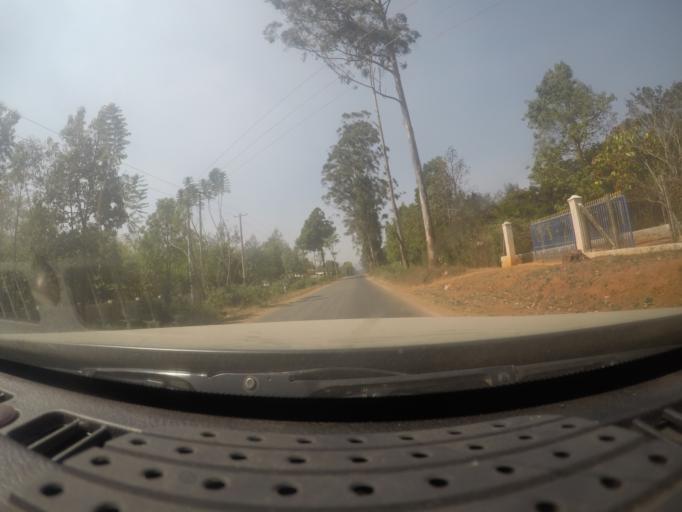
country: MM
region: Mandalay
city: Kyaukse
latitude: 21.1426
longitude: 96.4469
